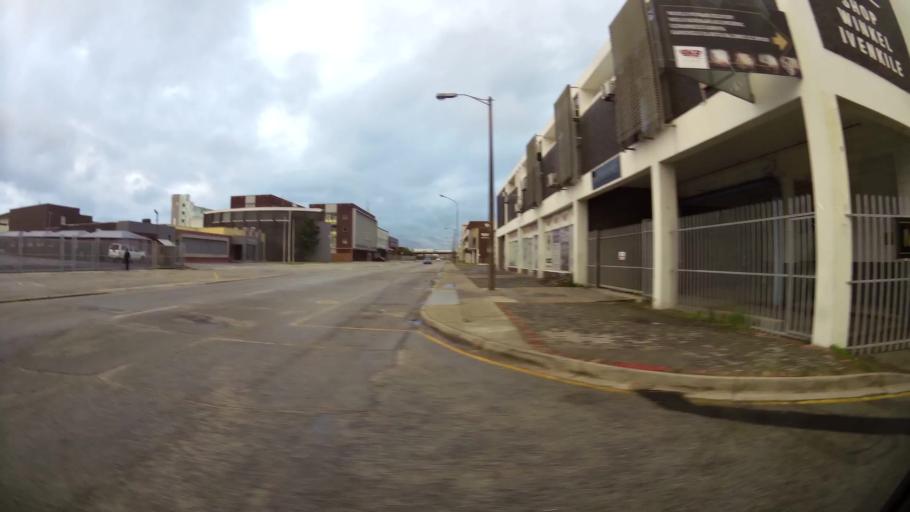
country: ZA
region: Eastern Cape
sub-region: Nelson Mandela Bay Metropolitan Municipality
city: Port Elizabeth
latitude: -33.9344
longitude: 25.6047
